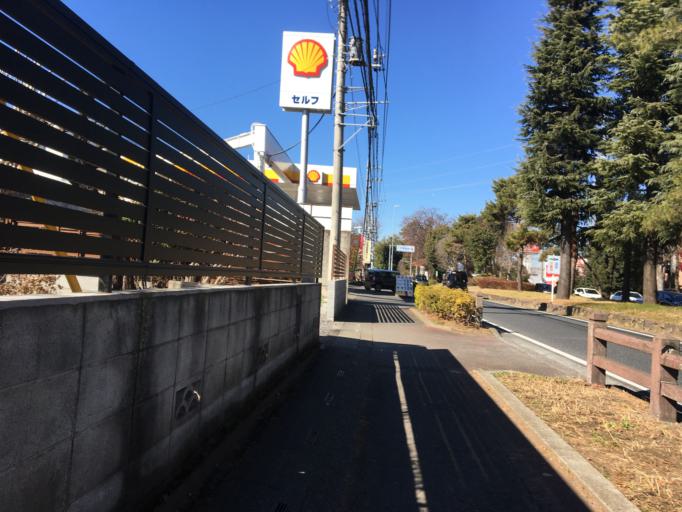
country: JP
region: Saitama
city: Oi
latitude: 35.8422
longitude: 139.5231
